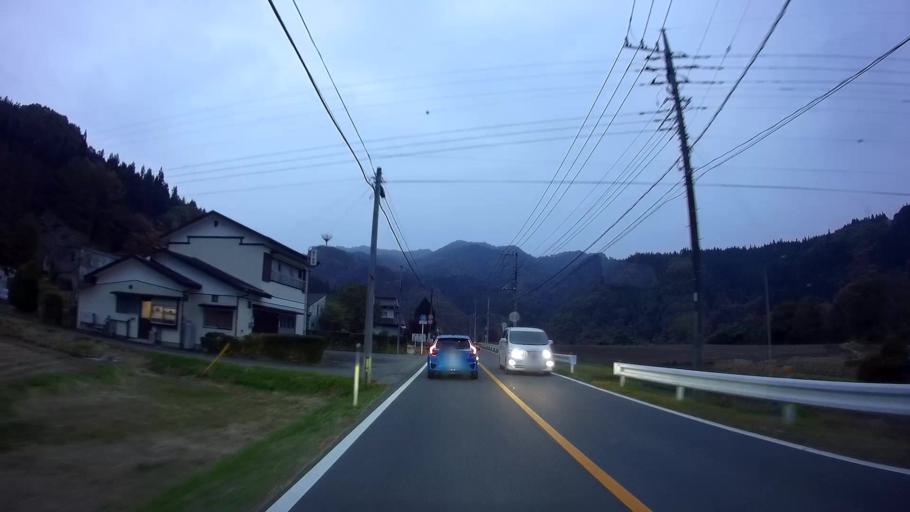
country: JP
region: Gunma
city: Nakanojomachi
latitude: 36.5333
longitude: 138.7837
